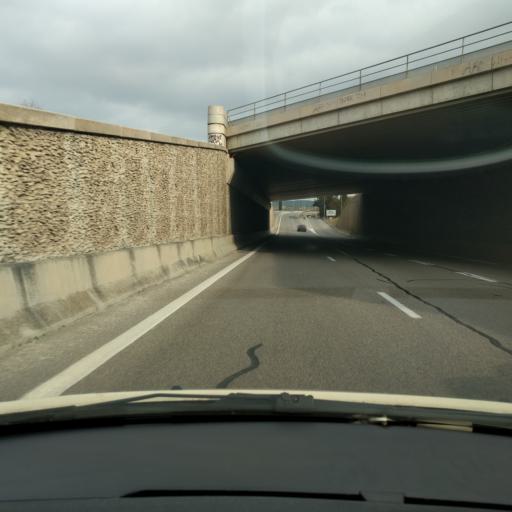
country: FR
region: Provence-Alpes-Cote d'Azur
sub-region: Departement des Bouches-du-Rhone
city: Gardanne
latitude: 43.4619
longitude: 5.4660
